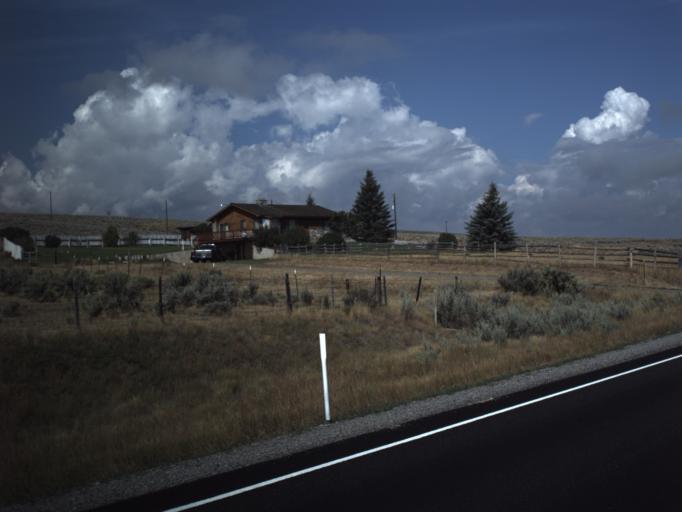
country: US
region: Utah
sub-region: Rich County
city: Randolph
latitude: 41.6083
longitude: -111.1782
